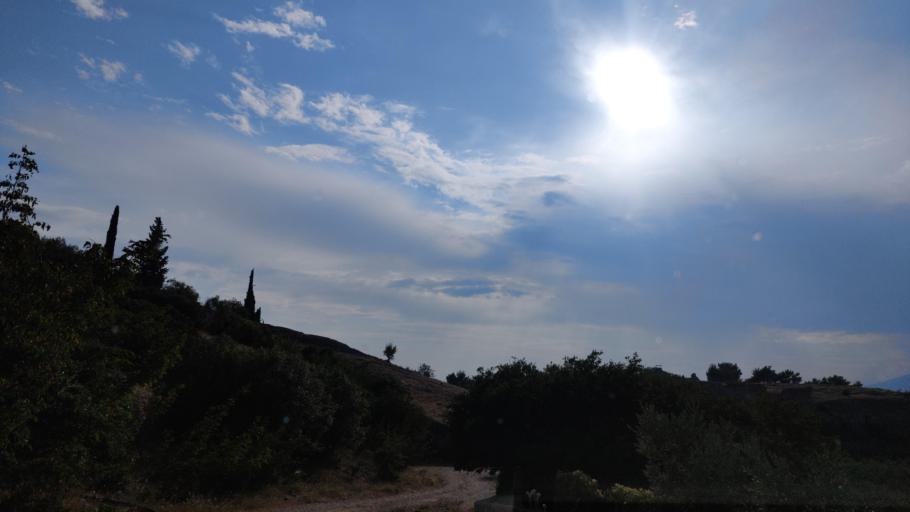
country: GR
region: Central Macedonia
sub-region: Nomos Serron
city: Sidirokastro
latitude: 41.2390
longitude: 23.4005
